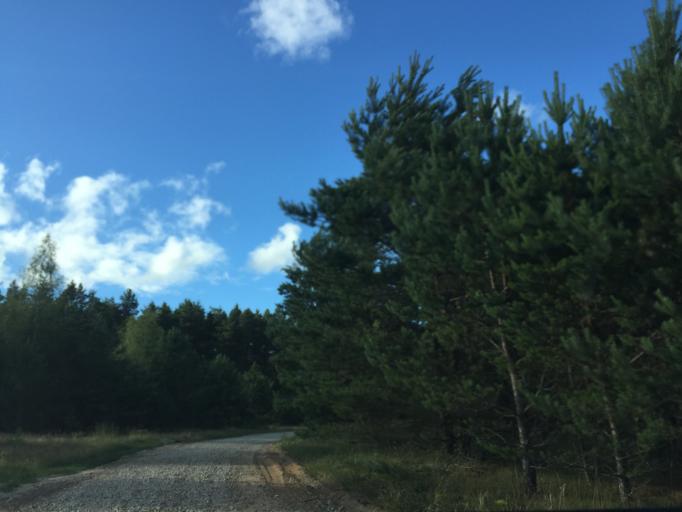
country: LV
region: Adazi
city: Adazi
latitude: 57.1312
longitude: 24.3459
